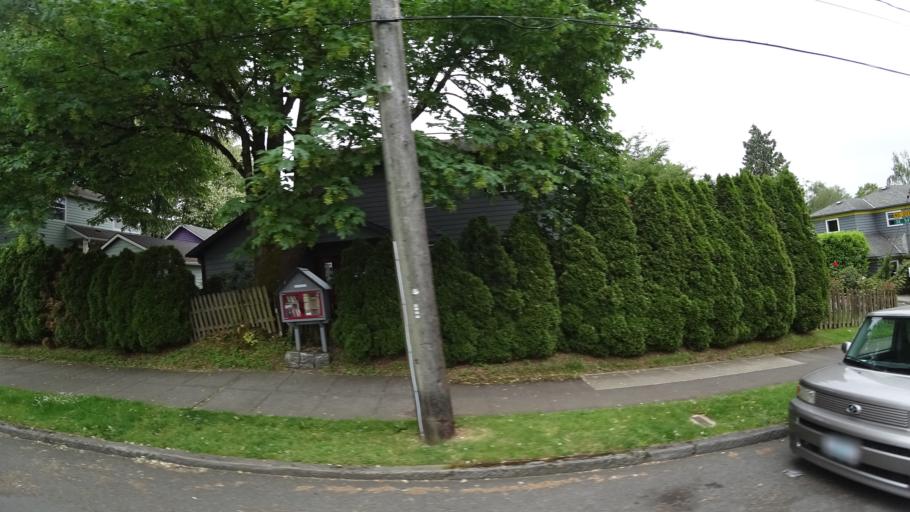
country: US
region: Oregon
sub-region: Multnomah County
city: Lents
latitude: 45.5193
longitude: -122.6031
